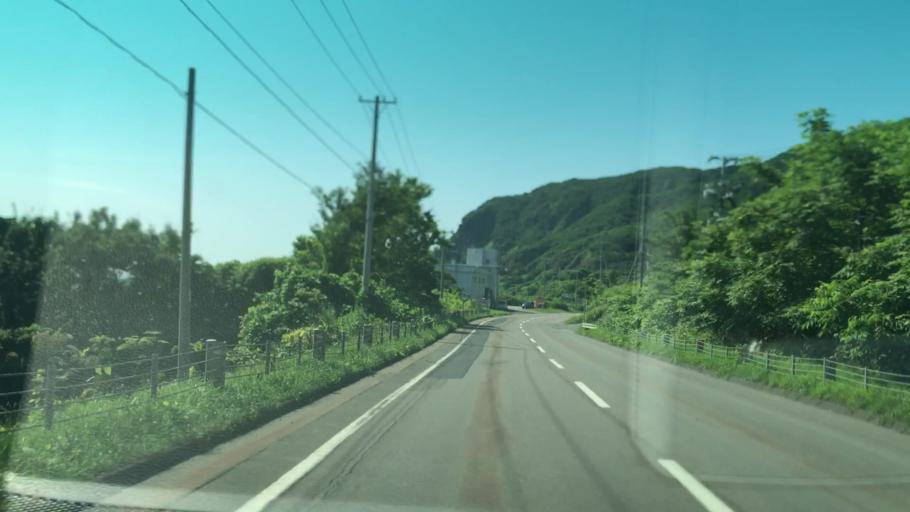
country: JP
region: Hokkaido
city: Iwanai
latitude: 43.0787
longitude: 140.4818
